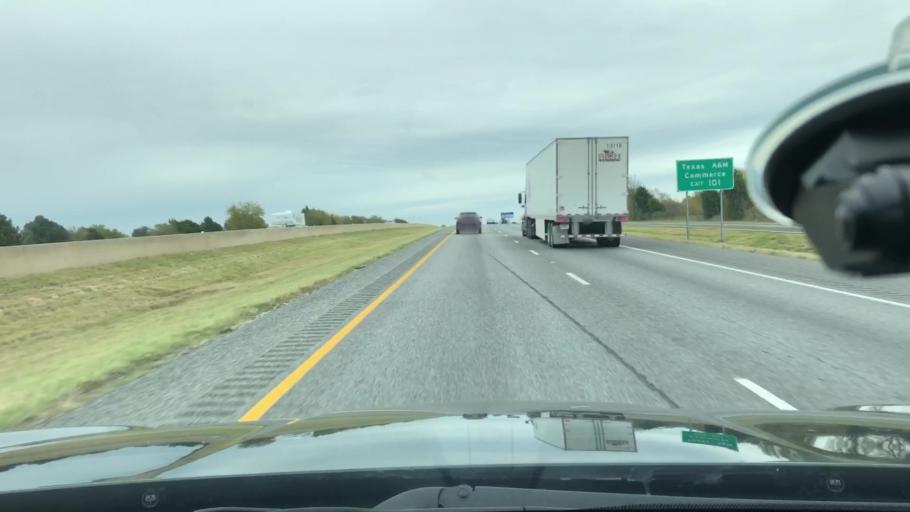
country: US
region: Texas
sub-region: Hunt County
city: Greenville
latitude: 33.1318
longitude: -96.0112
